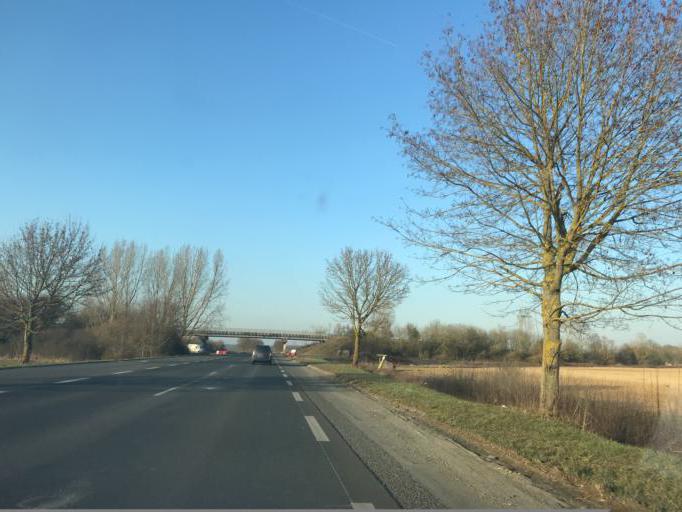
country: FR
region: Ile-de-France
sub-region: Departement de Seine-et-Marne
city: La Houssaye-en-Brie
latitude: 48.7468
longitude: 2.8578
